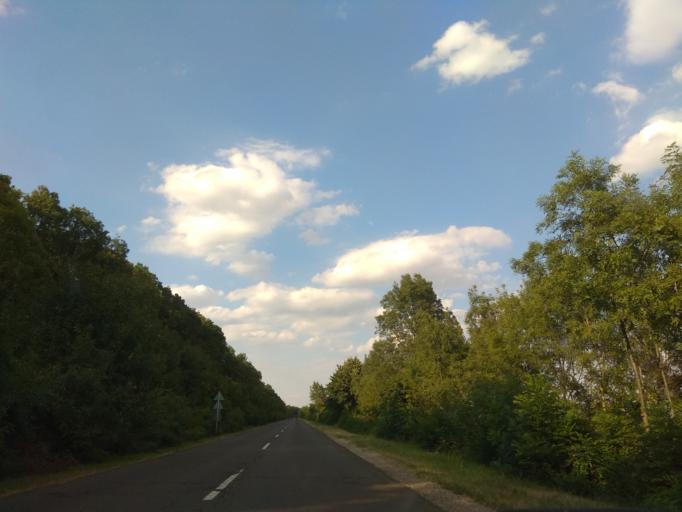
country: HU
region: Borsod-Abauj-Zemplen
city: Harsany
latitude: 47.9232
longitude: 20.7227
